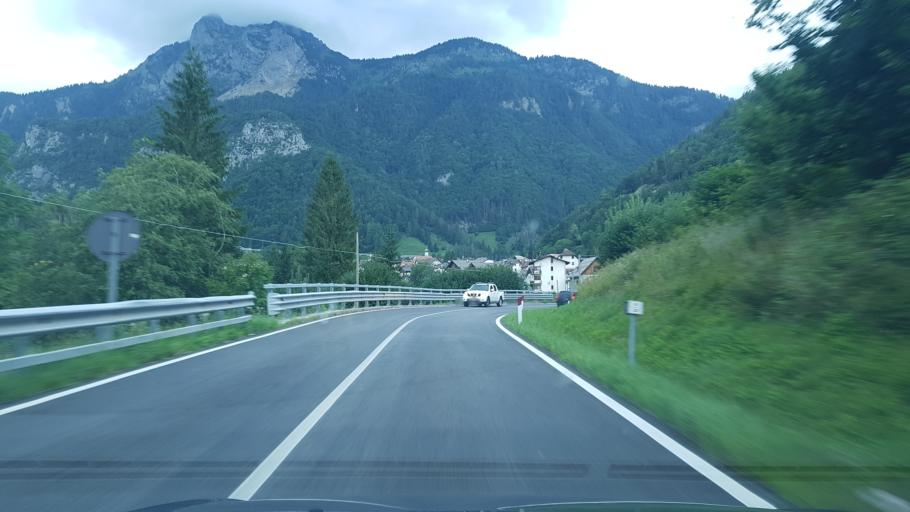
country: IT
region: Friuli Venezia Giulia
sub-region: Provincia di Udine
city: Forni Avoltri
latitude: 46.5819
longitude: 12.7835
